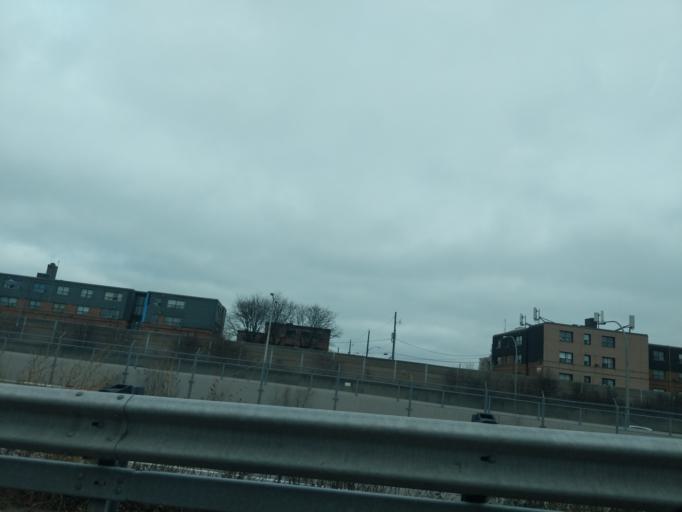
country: CA
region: Ontario
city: Toronto
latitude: 43.7174
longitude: -79.4451
